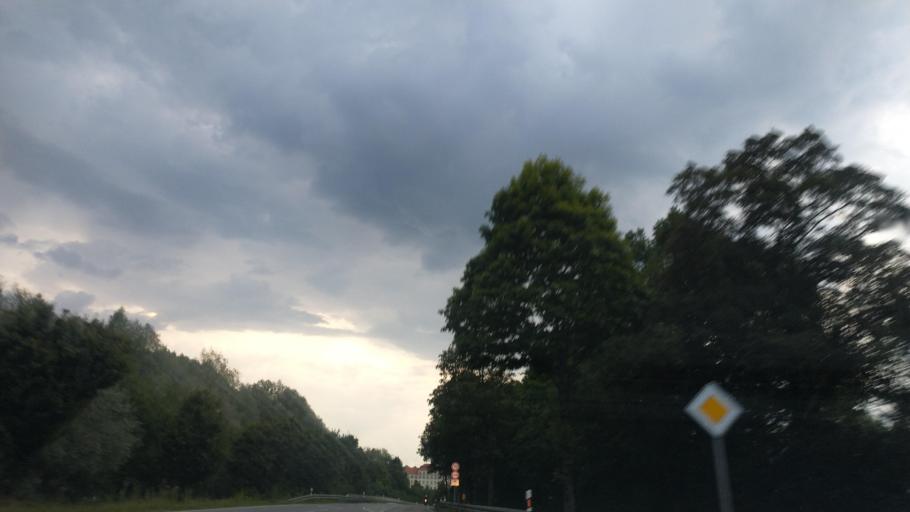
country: DE
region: Baden-Wuerttemberg
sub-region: Tuebingen Region
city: Tettnang
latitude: 47.6659
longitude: 9.5763
